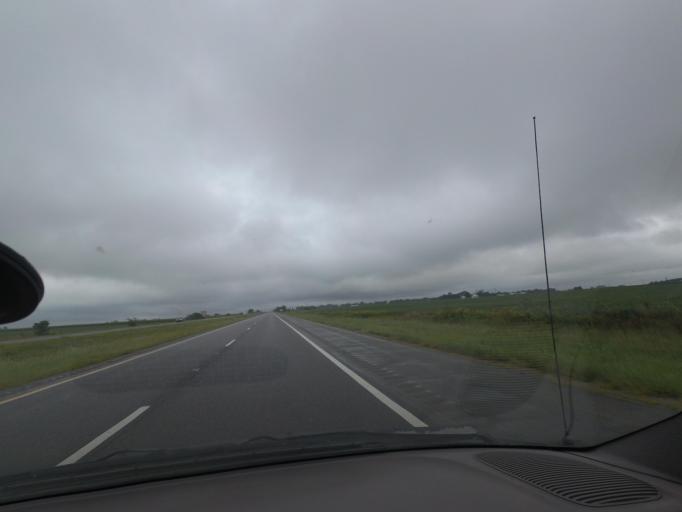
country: US
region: Illinois
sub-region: Champaign County
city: Mahomet
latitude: 40.1203
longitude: -88.3869
